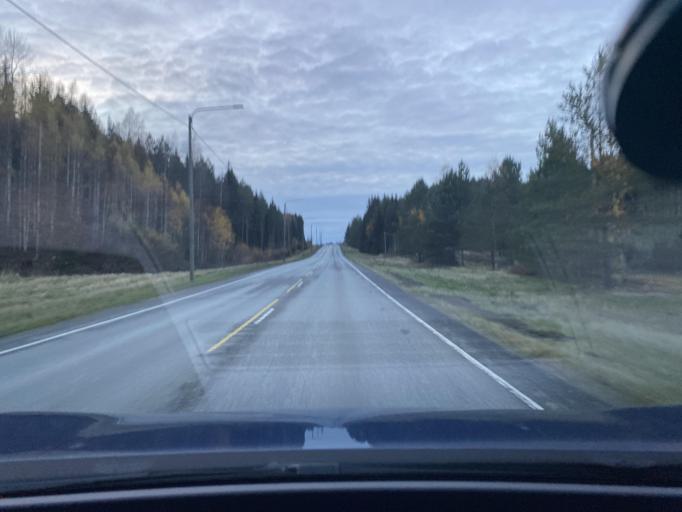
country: FI
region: Uusimaa
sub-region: Helsinki
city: Saukkola
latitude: 60.3867
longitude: 24.0579
